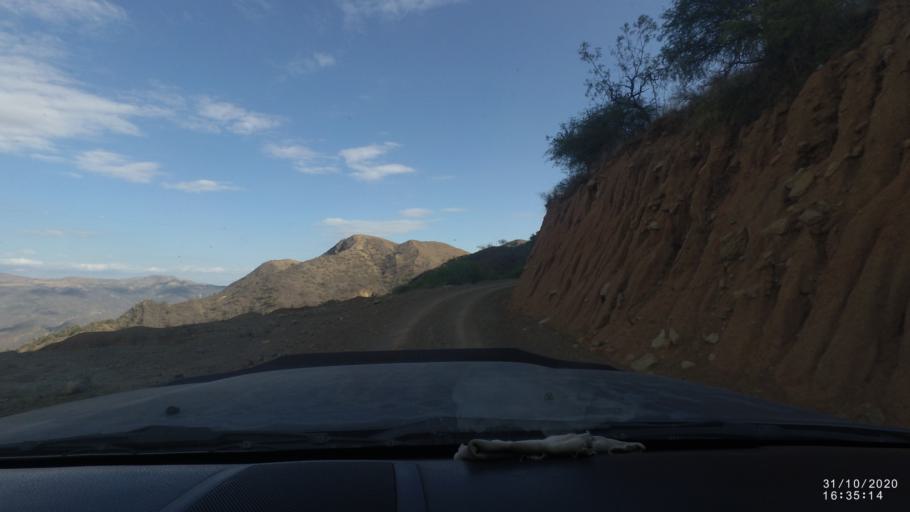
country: BO
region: Chuquisaca
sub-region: Provincia Zudanez
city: Mojocoya
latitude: -18.4532
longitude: -64.5832
